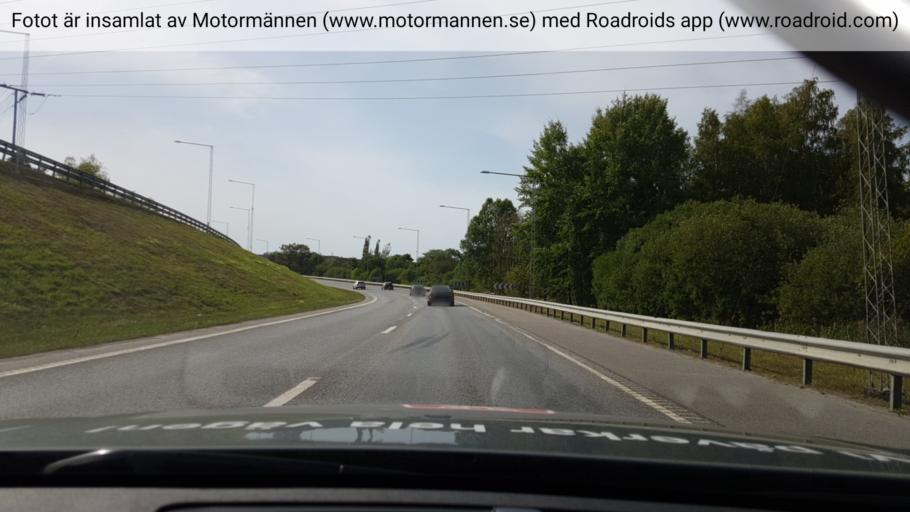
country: SE
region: Stockholm
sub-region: Nacka Kommun
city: Alta
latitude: 59.2642
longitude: 18.1491
